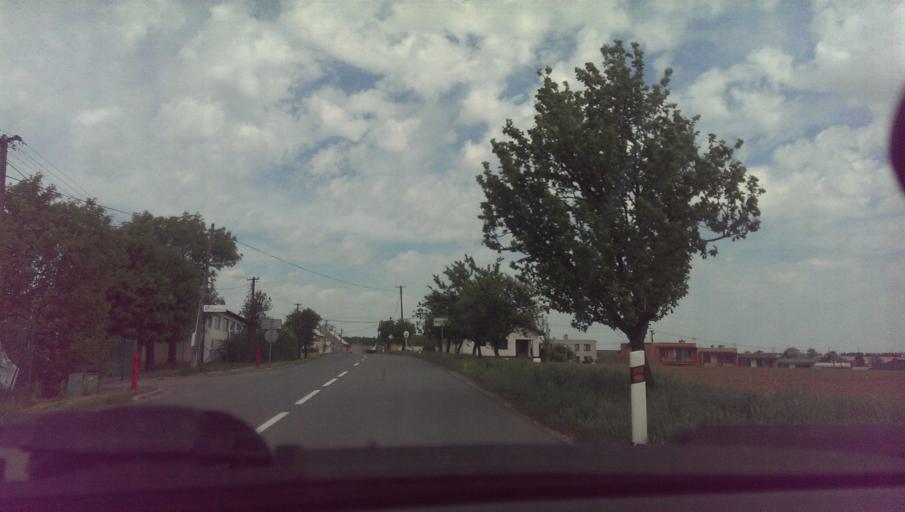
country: CZ
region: Zlin
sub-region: Okres Zlin
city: Otrokovice
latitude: 49.2503
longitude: 17.5432
